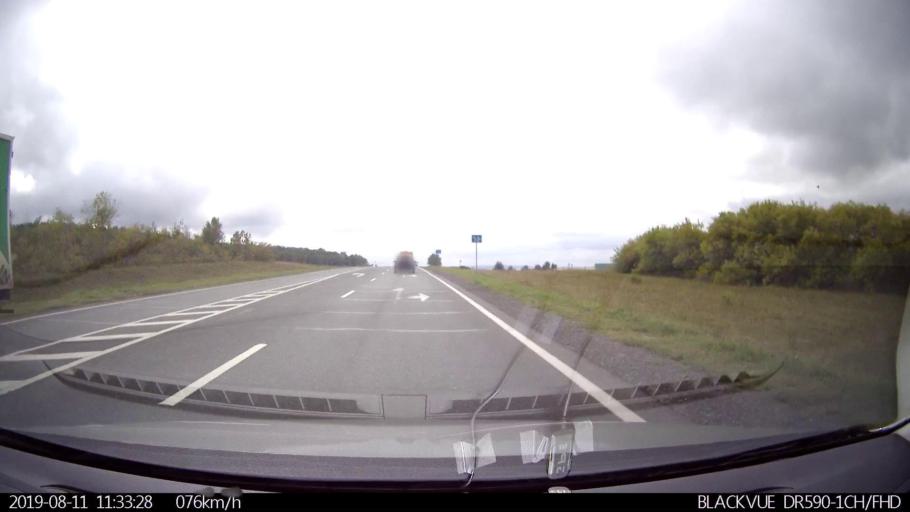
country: RU
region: Ulyanovsk
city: Krasnyy Gulyay
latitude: 54.0270
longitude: 48.2128
